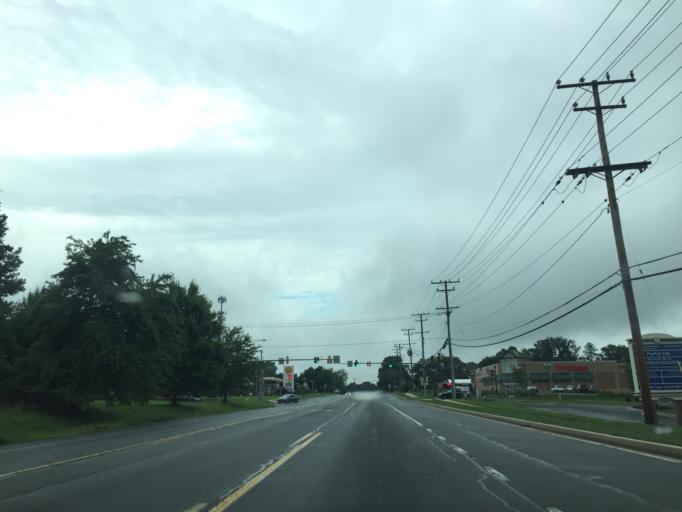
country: US
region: Maryland
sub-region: Harford County
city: Bel Air South
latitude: 39.5018
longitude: -76.3264
